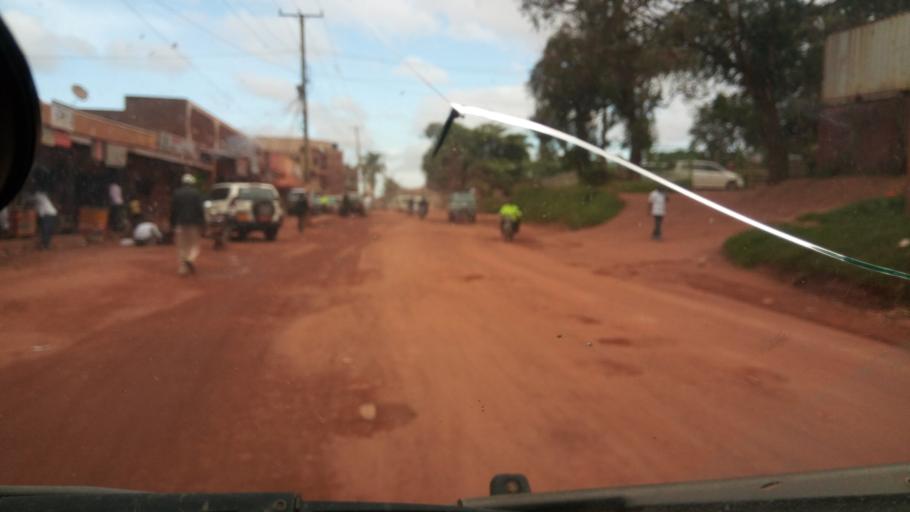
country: UG
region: Central Region
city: Kampala Central Division
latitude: 0.3231
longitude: 32.5618
